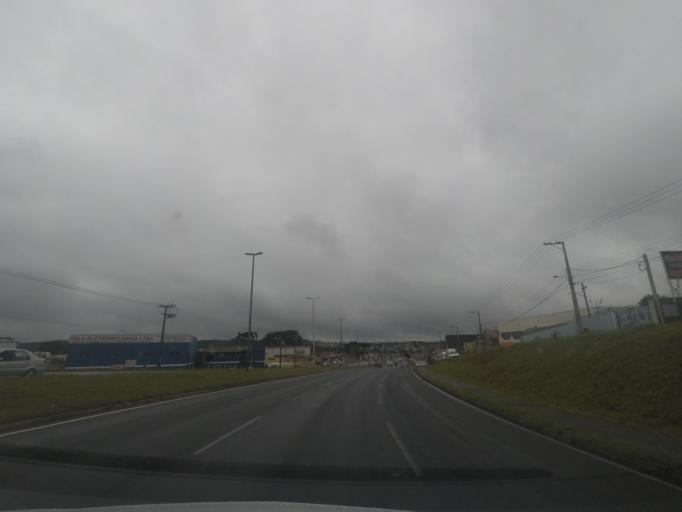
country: BR
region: Parana
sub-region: Colombo
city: Colombo
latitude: -25.3531
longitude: -49.1797
